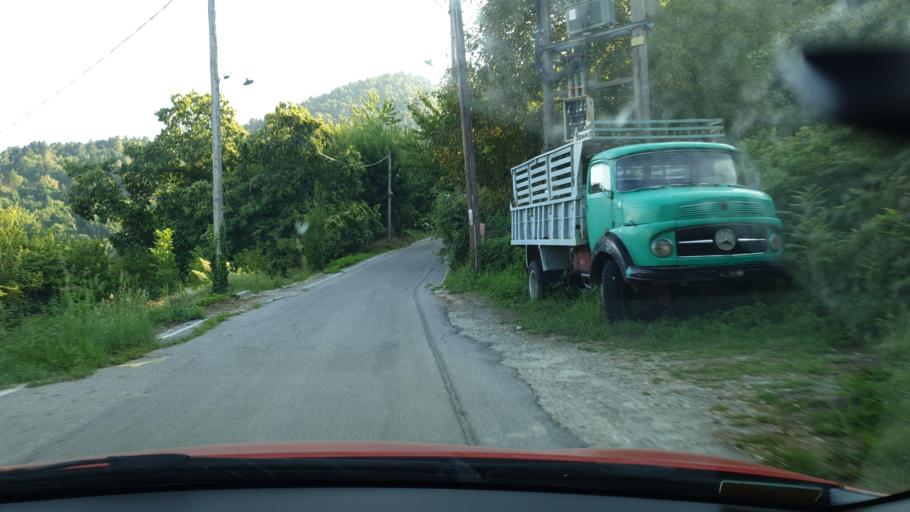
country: GR
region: Central Greece
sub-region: Nomos Evvoias
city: Kymi
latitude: 38.6407
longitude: 23.9363
